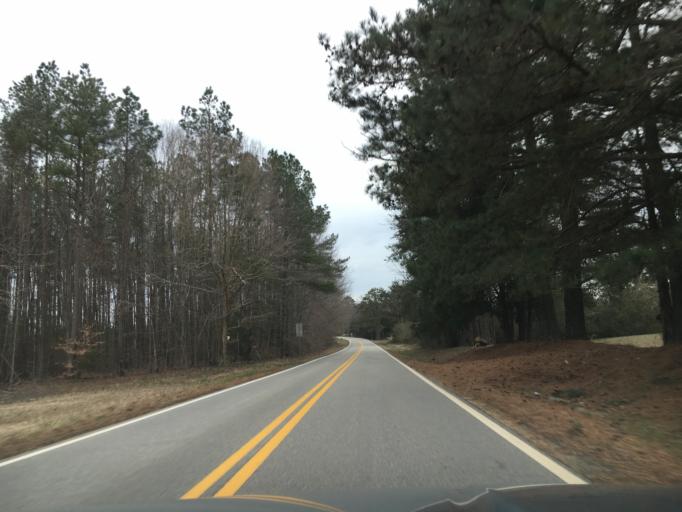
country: US
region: Virginia
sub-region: Charlotte County
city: Charlotte Court House
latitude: 36.9795
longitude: -78.6980
